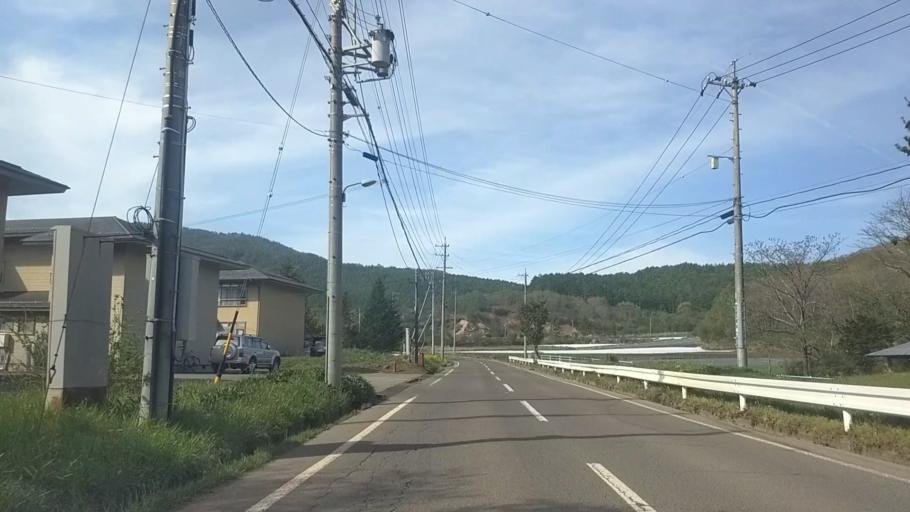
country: JP
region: Yamanashi
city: Nirasaki
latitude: 35.9406
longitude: 138.4668
